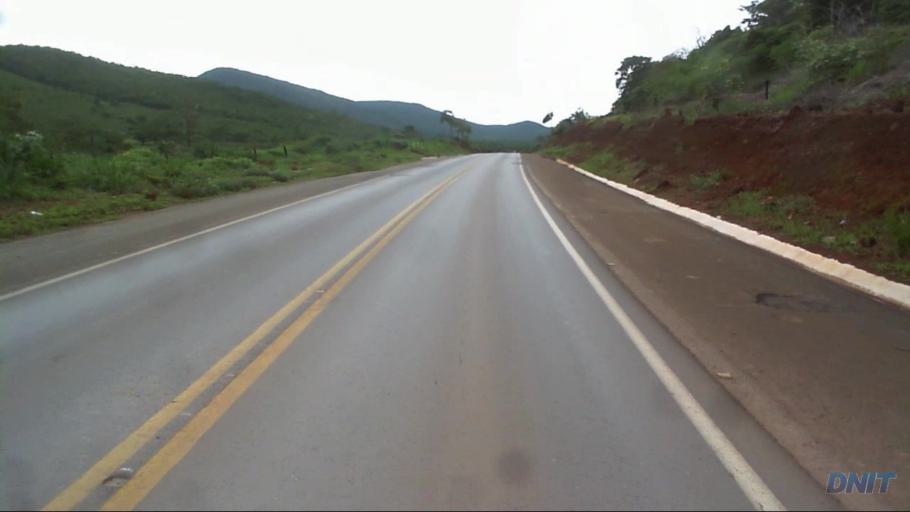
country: BR
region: Goias
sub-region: Barro Alto
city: Barro Alto
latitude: -14.8860
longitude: -48.9808
